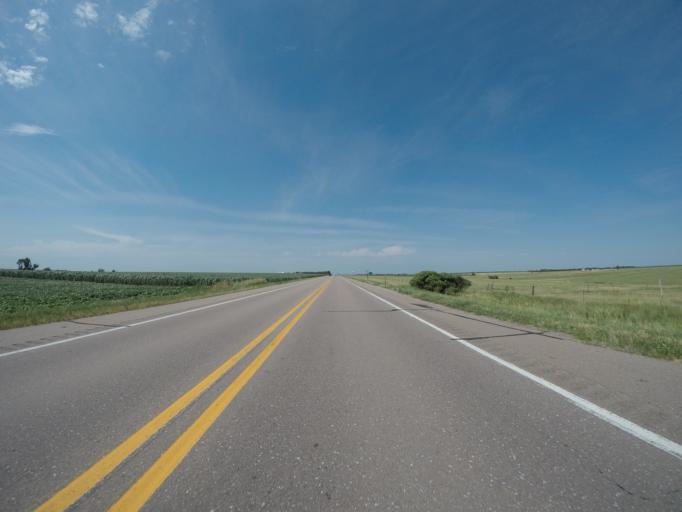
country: US
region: Nebraska
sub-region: Webster County
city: Red Cloud
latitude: 40.2991
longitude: -98.4439
